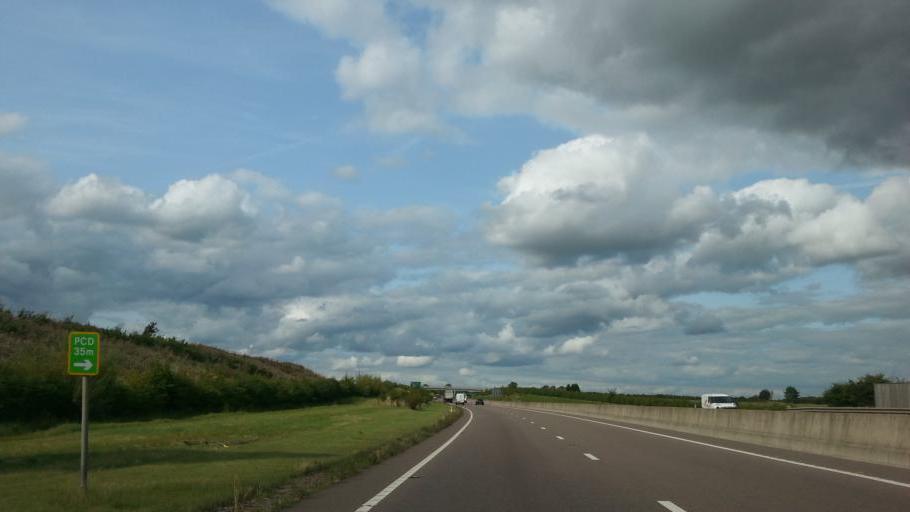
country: GB
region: England
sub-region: Nottinghamshire
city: Cropwell Bishop
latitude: 52.9352
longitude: -0.9938
